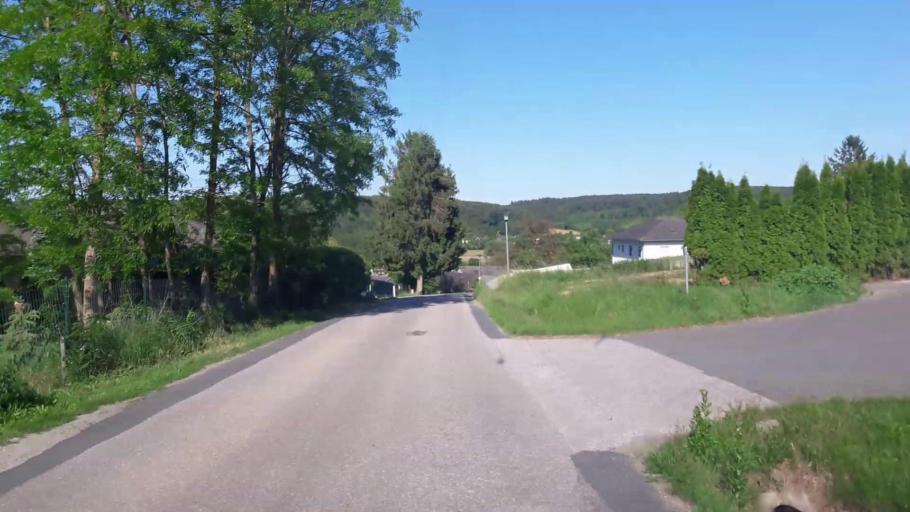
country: AT
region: Burgenland
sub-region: Politischer Bezirk Gussing
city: Ollersdorf im Burgenland
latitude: 47.1751
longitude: 16.1525
